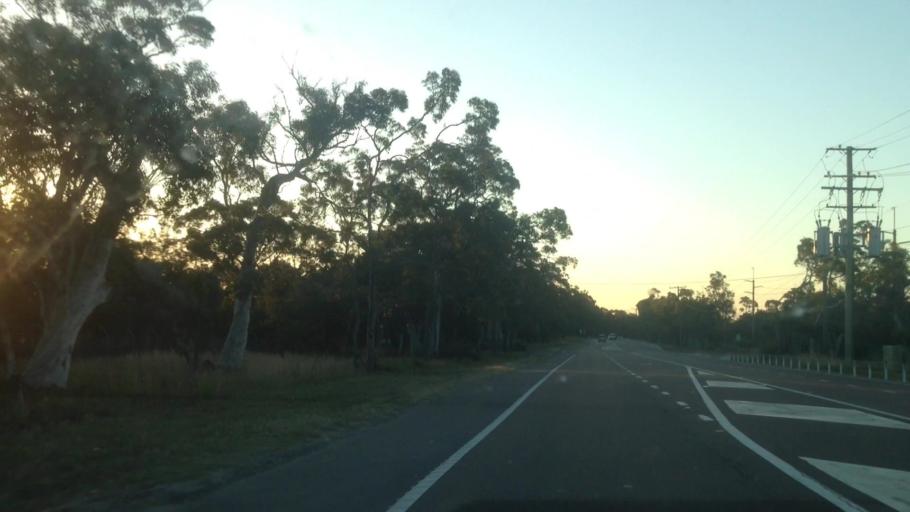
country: AU
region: New South Wales
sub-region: Wyong Shire
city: Kingfisher Shores
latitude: -33.1718
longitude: 151.5375
